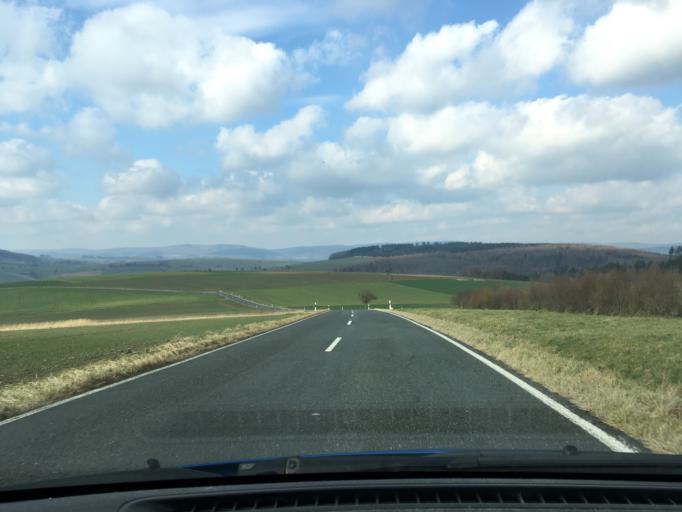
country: DE
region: Lower Saxony
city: Uslar
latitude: 51.6119
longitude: 9.6313
